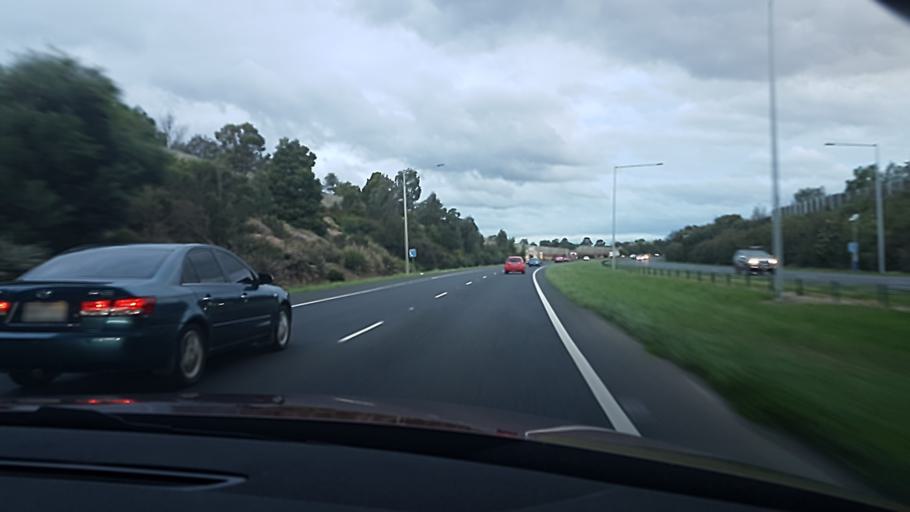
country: AU
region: Victoria
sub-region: Casey
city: Narre Warren North
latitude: -38.0008
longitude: 145.2933
